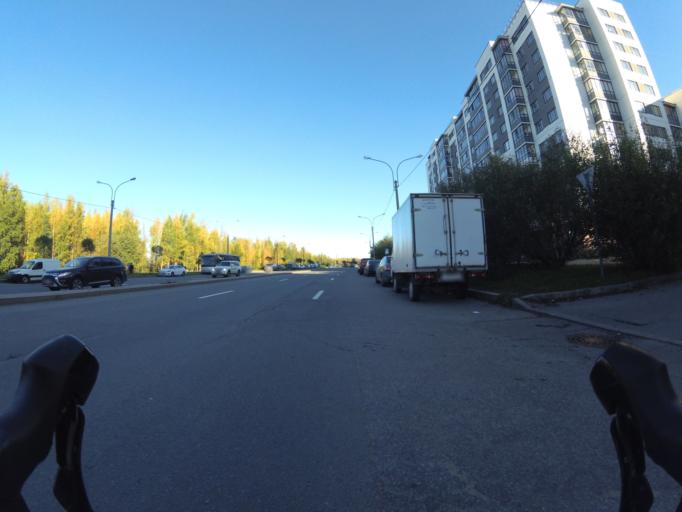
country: RU
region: Leningrad
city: Untolovo
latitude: 60.0063
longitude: 30.1981
